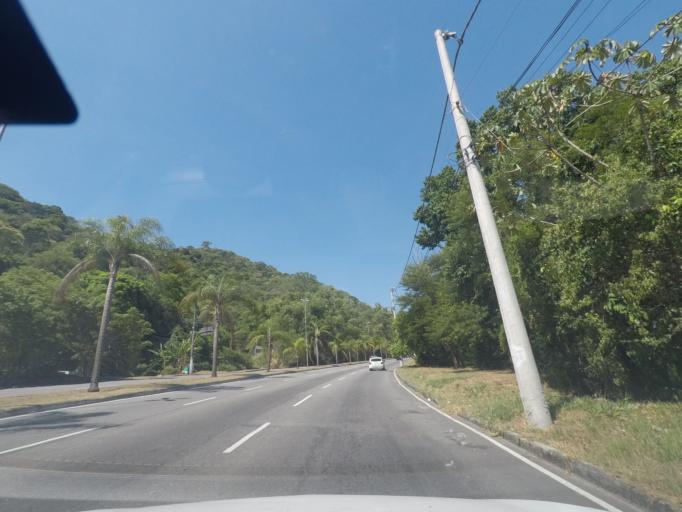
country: BR
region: Rio de Janeiro
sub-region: Niteroi
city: Niteroi
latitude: -22.9245
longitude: -43.0602
